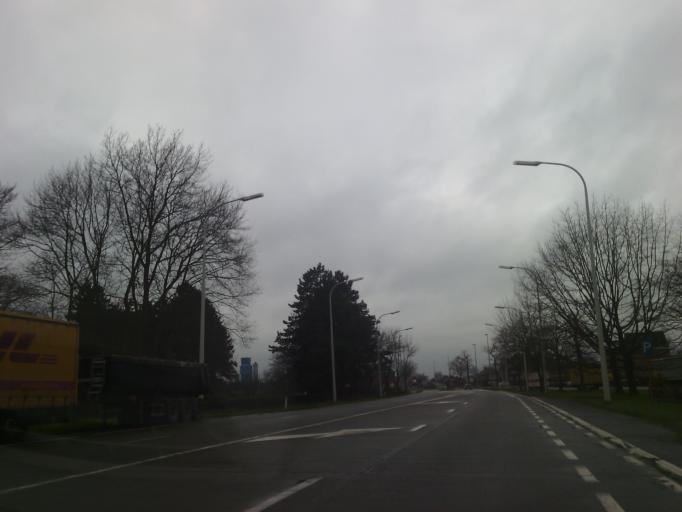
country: BE
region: Flanders
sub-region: Provincie Oost-Vlaanderen
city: Lochristi
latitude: 51.1074
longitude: 3.8857
